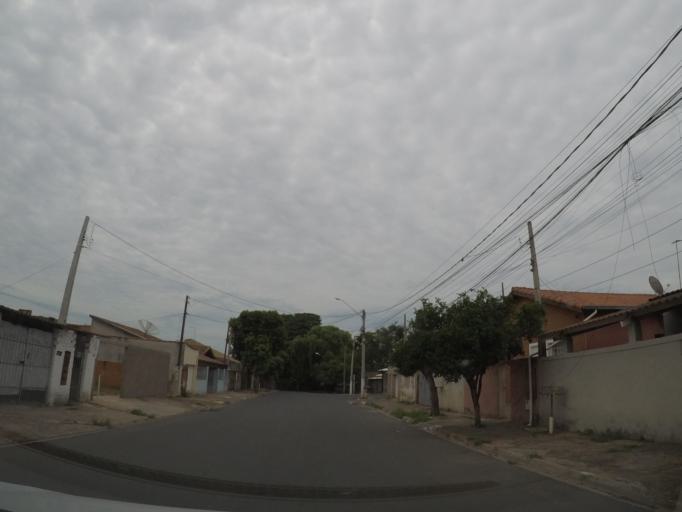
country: BR
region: Sao Paulo
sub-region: Hortolandia
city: Hortolandia
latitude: -22.8355
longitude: -47.1881
